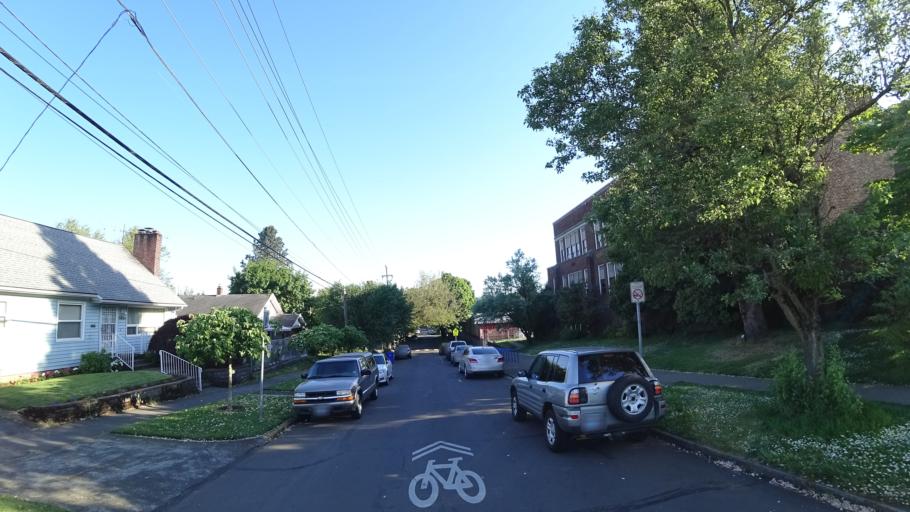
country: US
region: Oregon
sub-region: Multnomah County
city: Portland
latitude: 45.5583
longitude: -122.6849
